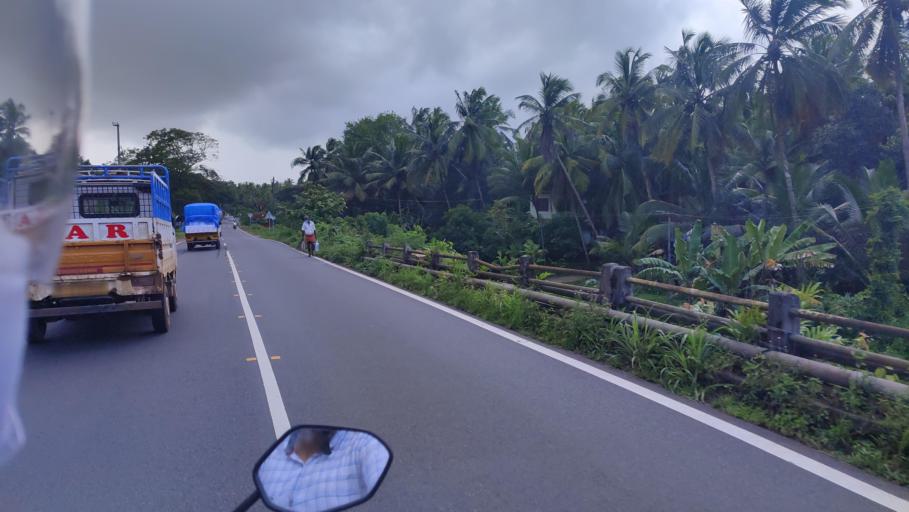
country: IN
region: Kerala
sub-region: Kasaragod District
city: Nileshwar
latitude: 12.2343
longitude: 75.1532
